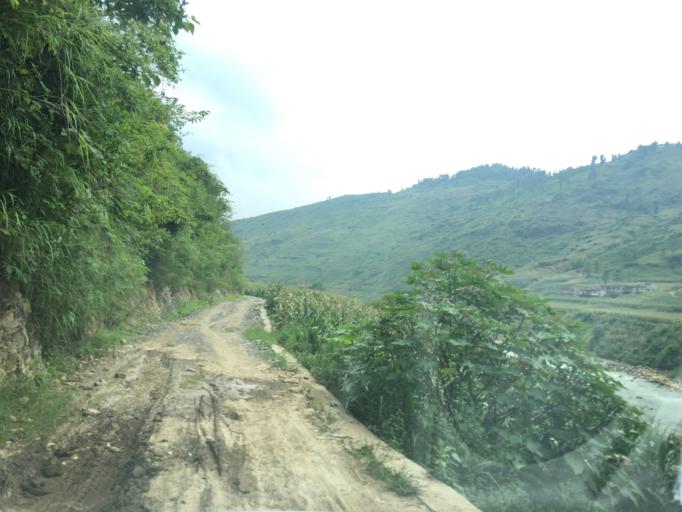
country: CN
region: Guangxi Zhuangzu Zizhiqu
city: Xinzhou
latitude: 25.1939
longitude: 105.7325
